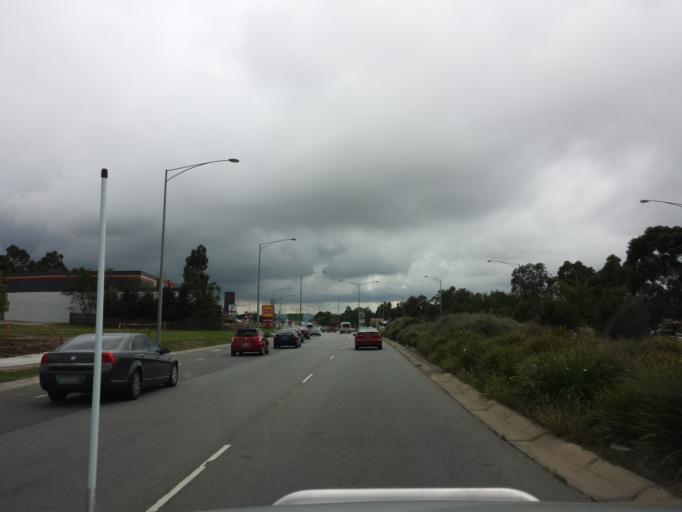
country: AU
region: Victoria
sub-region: Casey
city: Narre Warren
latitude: -38.0232
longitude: 145.3075
